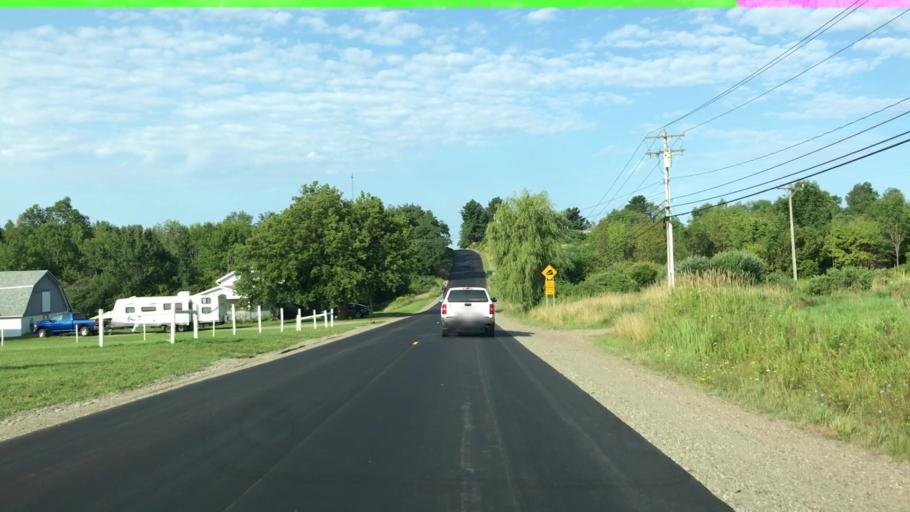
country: US
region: New York
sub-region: Chautauqua County
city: Fredonia
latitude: 42.3251
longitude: -79.3407
